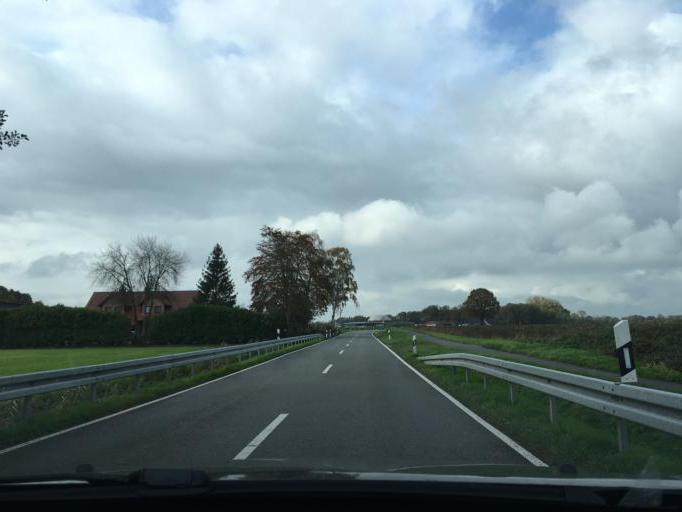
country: DE
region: North Rhine-Westphalia
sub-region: Regierungsbezirk Munster
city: Vreden
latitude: 52.0550
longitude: 6.7699
